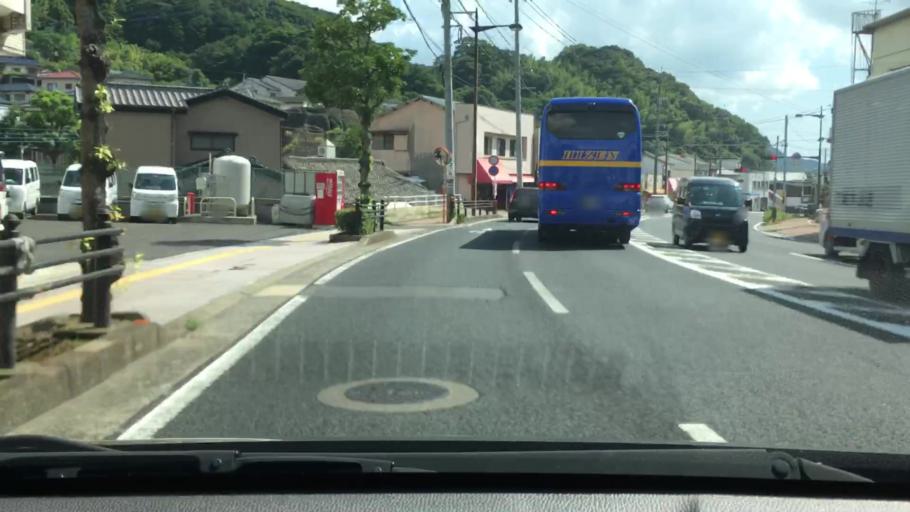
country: JP
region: Nagasaki
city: Sasebo
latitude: 33.1974
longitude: 129.7227
